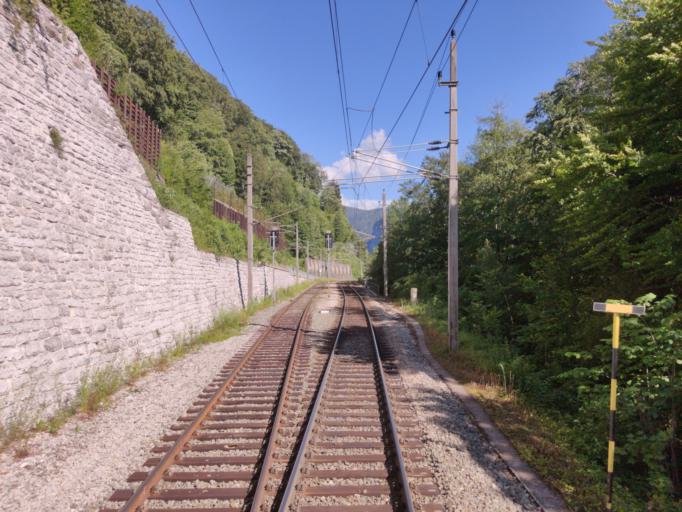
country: AT
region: Vorarlberg
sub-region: Politischer Bezirk Bludenz
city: Innerbraz
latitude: 47.1406
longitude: 9.9440
